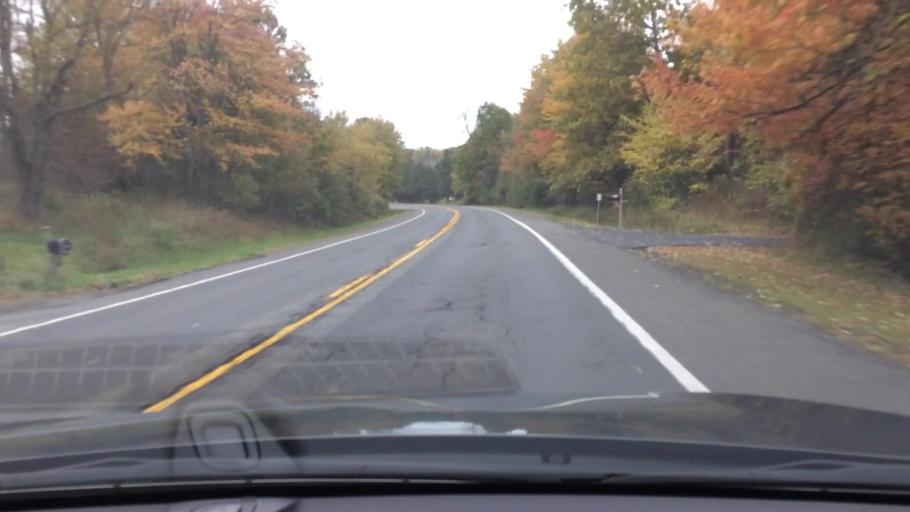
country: US
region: New York
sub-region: Columbia County
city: Oakdale
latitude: 42.1489
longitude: -73.7456
